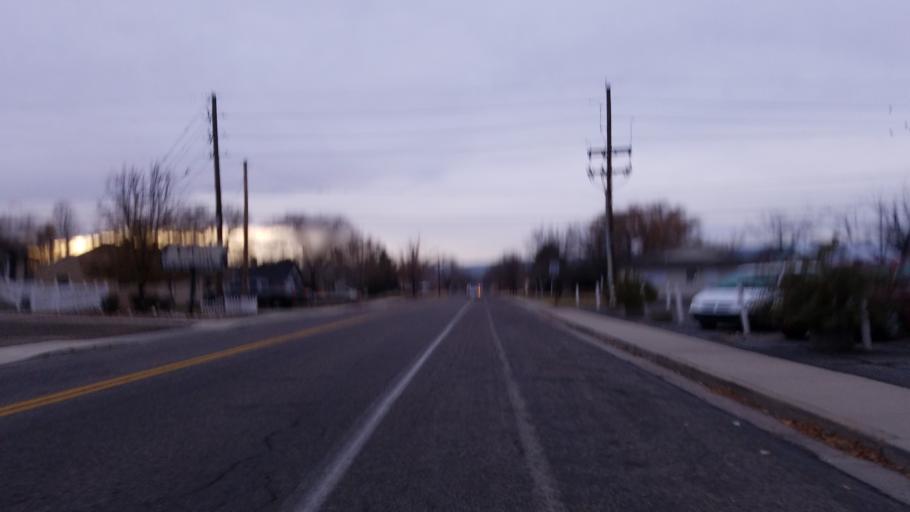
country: US
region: Colorado
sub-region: Mesa County
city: Grand Junction
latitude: 39.0773
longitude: -108.5679
